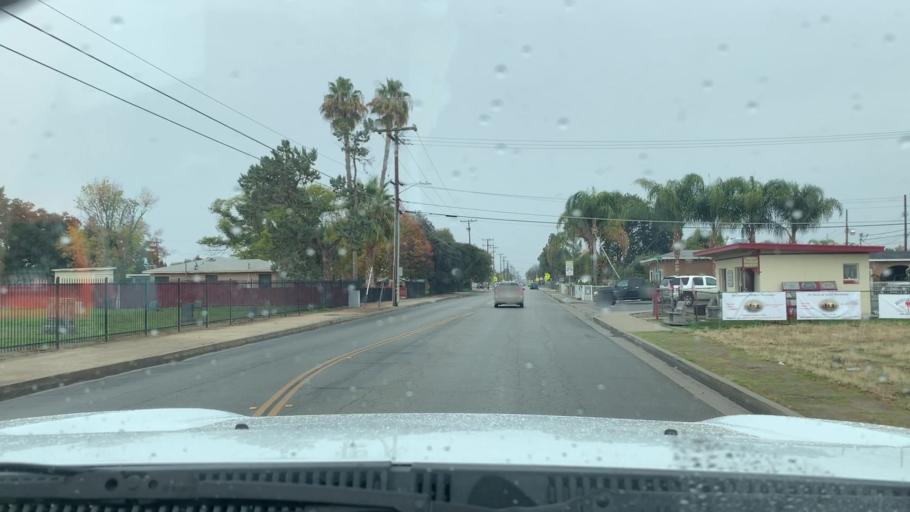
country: US
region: California
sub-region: Kern County
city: Delano
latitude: 35.7614
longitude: -119.2579
